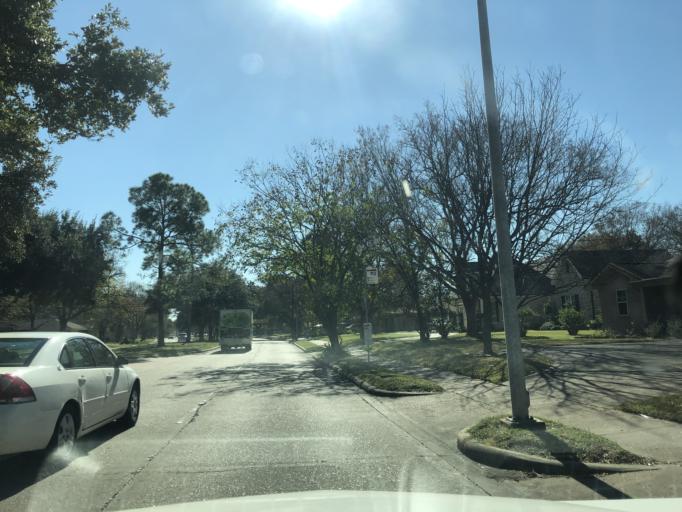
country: US
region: Texas
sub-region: Harris County
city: Bellaire
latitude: 29.6919
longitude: -95.4931
